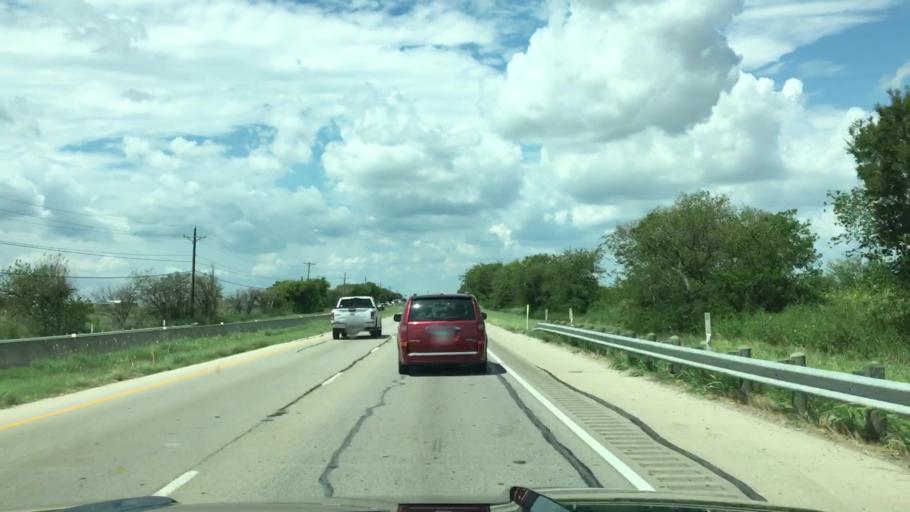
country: US
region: Texas
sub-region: Tarrant County
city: Saginaw
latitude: 32.8905
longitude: -97.3900
